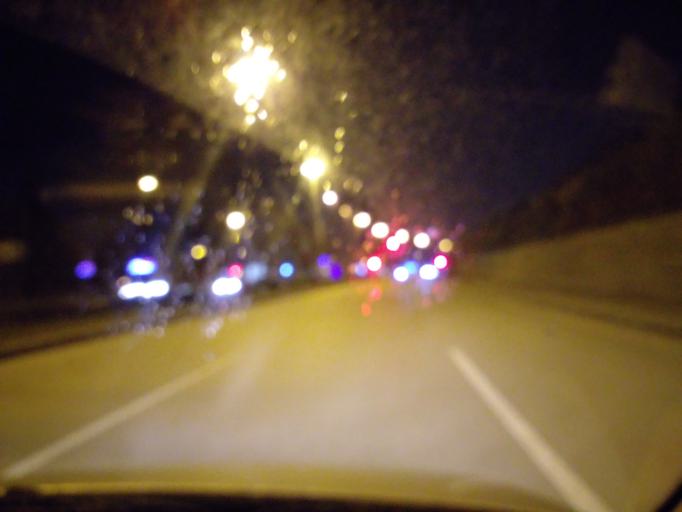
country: TR
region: Ankara
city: Batikent
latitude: 39.8893
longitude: 32.7206
